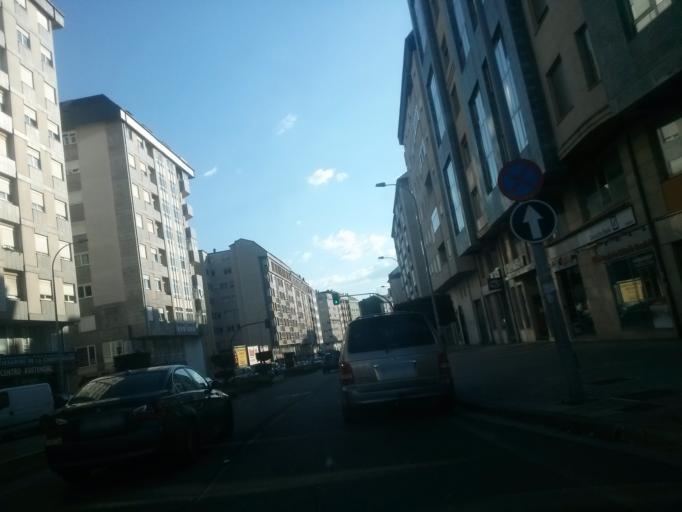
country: ES
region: Galicia
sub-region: Provincia de Lugo
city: Lugo
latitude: 43.0113
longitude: -7.5673
